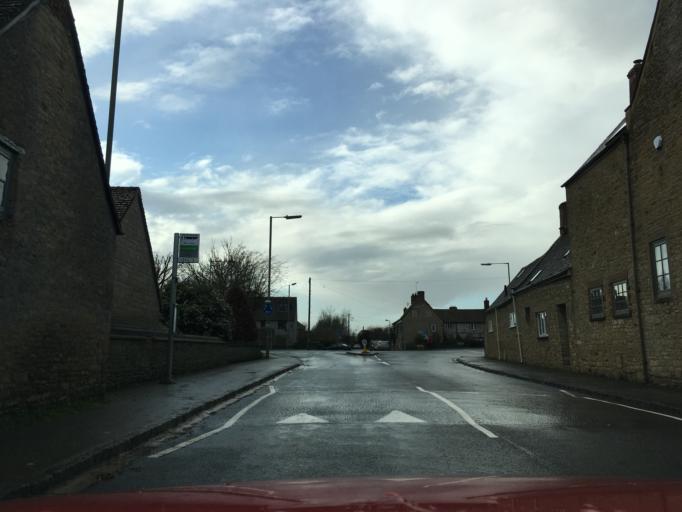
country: GB
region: England
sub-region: Oxfordshire
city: Eynsham
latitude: 51.7807
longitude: -1.3794
